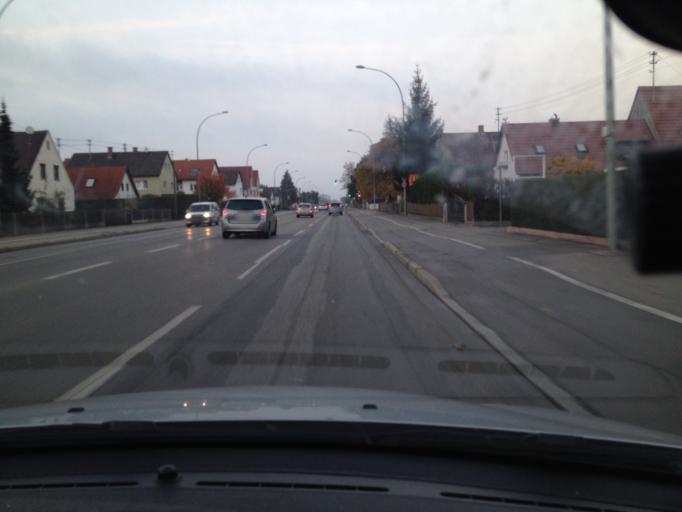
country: DE
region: Bavaria
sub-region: Swabia
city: Konigsbrunn
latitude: 48.2877
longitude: 10.8960
